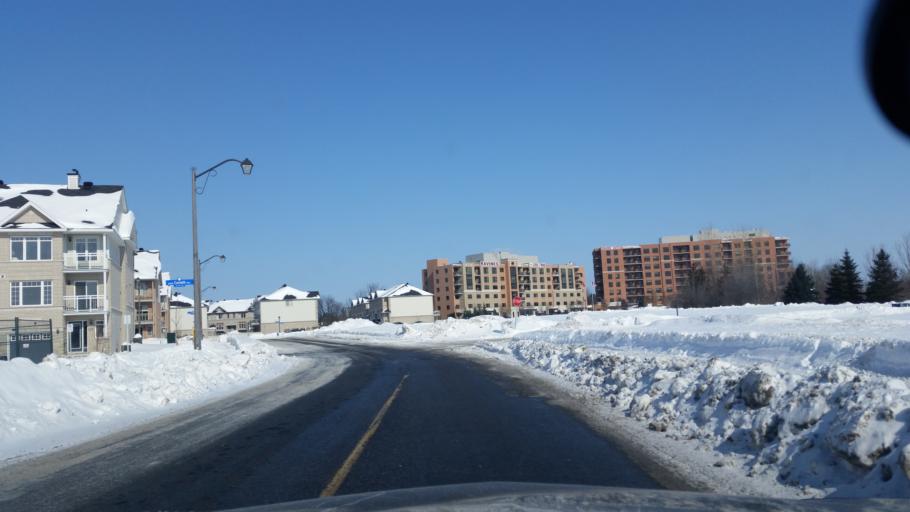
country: CA
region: Ontario
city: Ottawa
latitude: 45.3475
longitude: -75.7077
